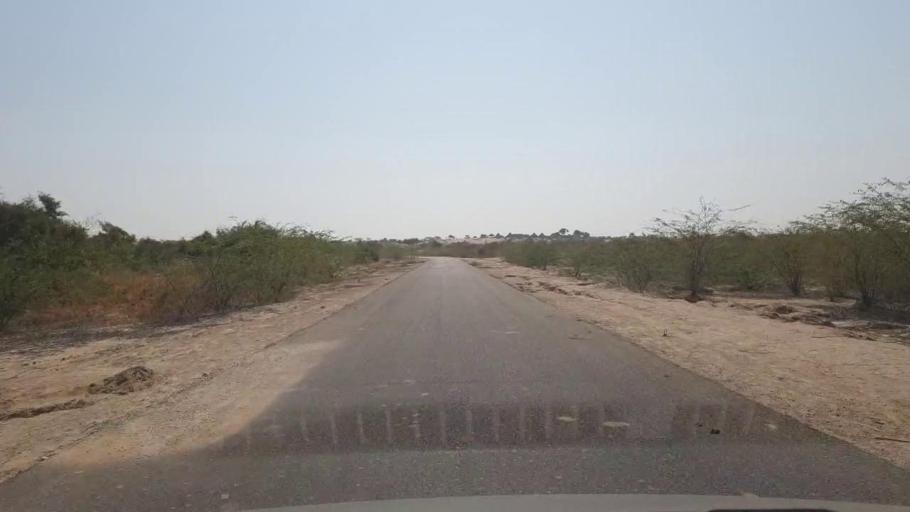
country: PK
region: Sindh
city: Chor
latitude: 25.5874
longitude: 70.1846
